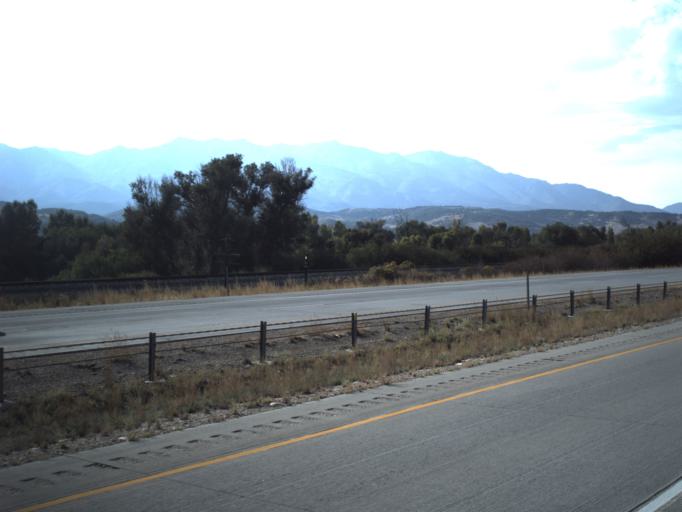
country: US
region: Utah
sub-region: Morgan County
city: Morgan
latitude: 41.0809
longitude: -111.7270
